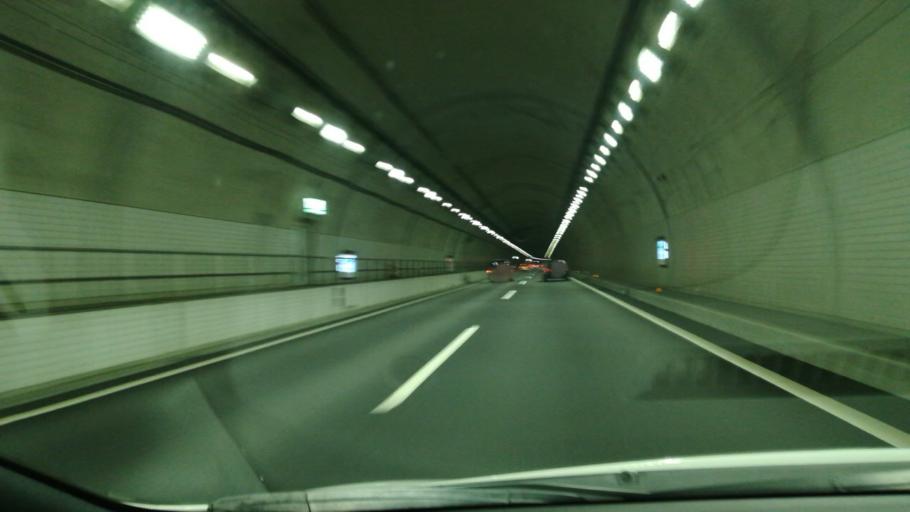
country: JP
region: Tokyo
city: Hachioji
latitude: 35.5969
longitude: 139.2775
